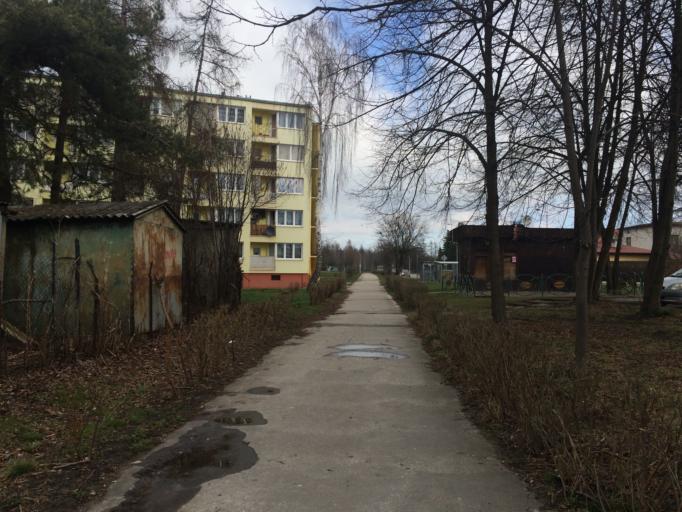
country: PL
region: Swietokrzyskie
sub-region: Powiat starachowicki
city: Starachowice
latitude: 51.0565
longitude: 21.0756
